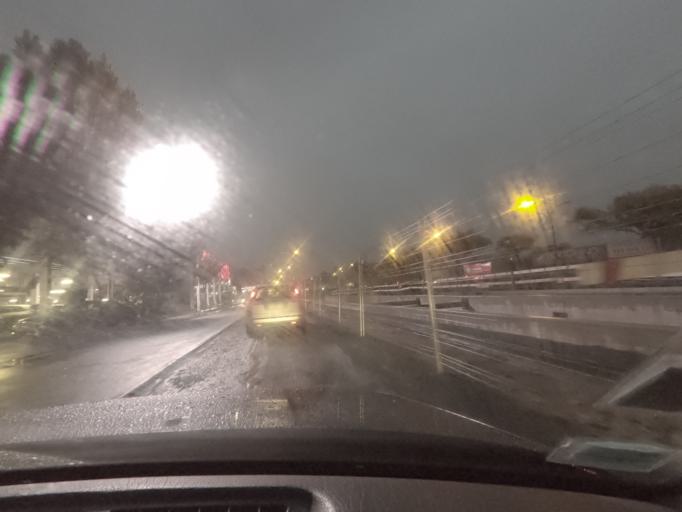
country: PT
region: Porto
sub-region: Matosinhos
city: Senhora da Hora
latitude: 41.1822
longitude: -8.6599
